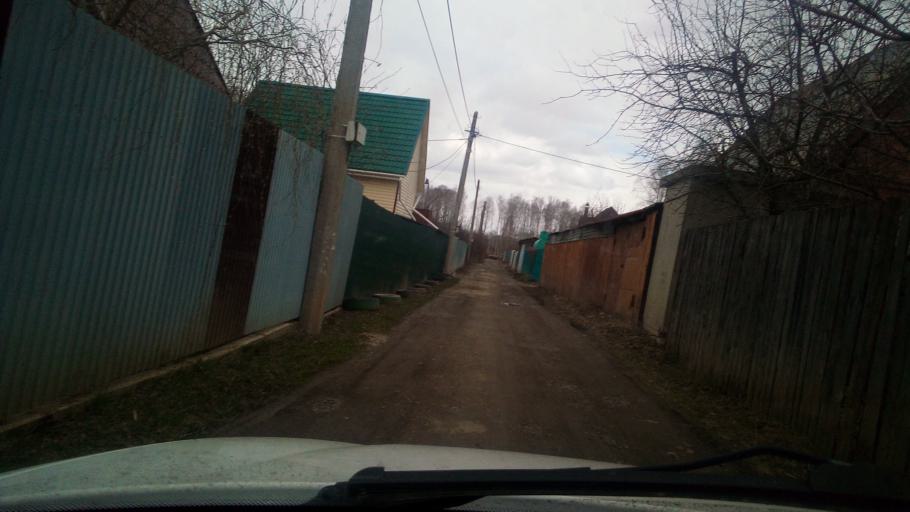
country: RU
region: Chelyabinsk
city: Sargazy
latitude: 55.1286
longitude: 61.2431
